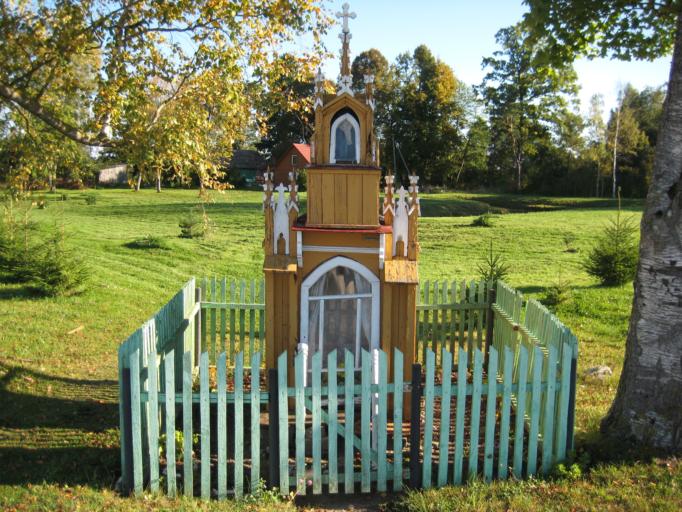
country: LT
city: Plateliai
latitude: 56.1519
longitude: 21.7362
